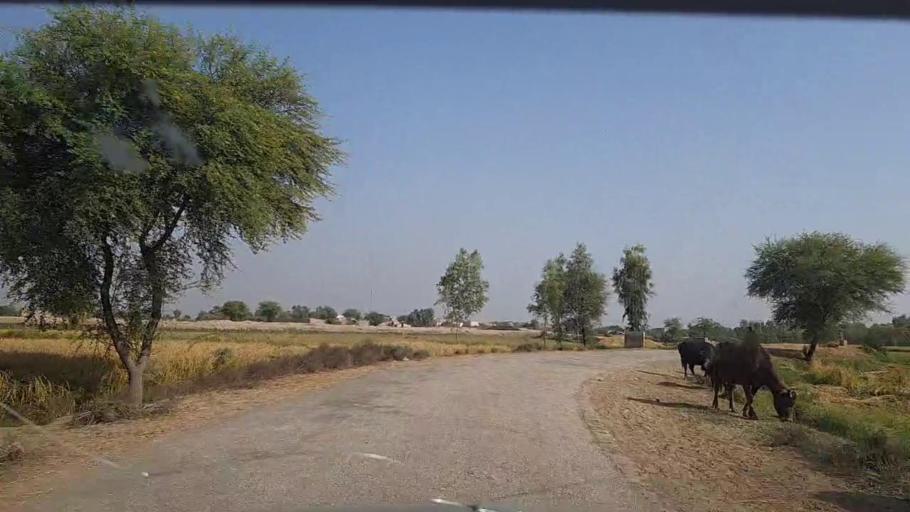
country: PK
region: Sindh
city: Shikarpur
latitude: 28.1169
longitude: 68.5755
